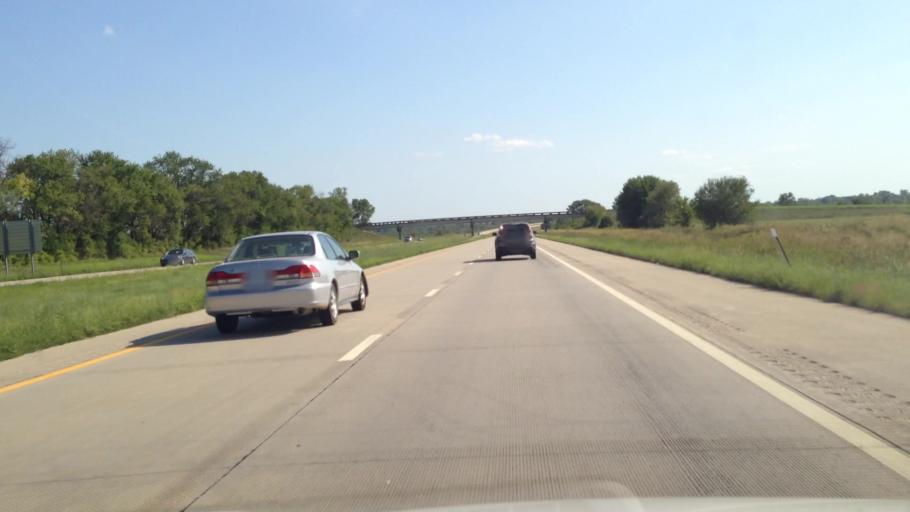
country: US
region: Kansas
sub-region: Bourbon County
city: Fort Scott
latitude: 37.9825
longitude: -94.7046
